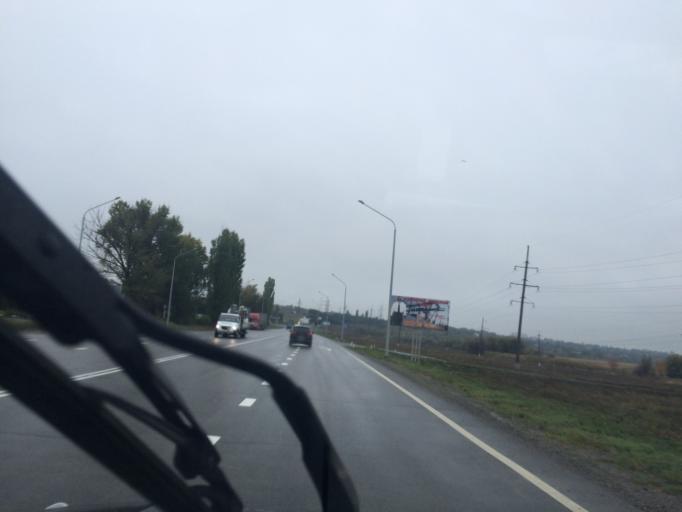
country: RU
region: Rostov
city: Kuleshovka
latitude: 47.0846
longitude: 39.4856
